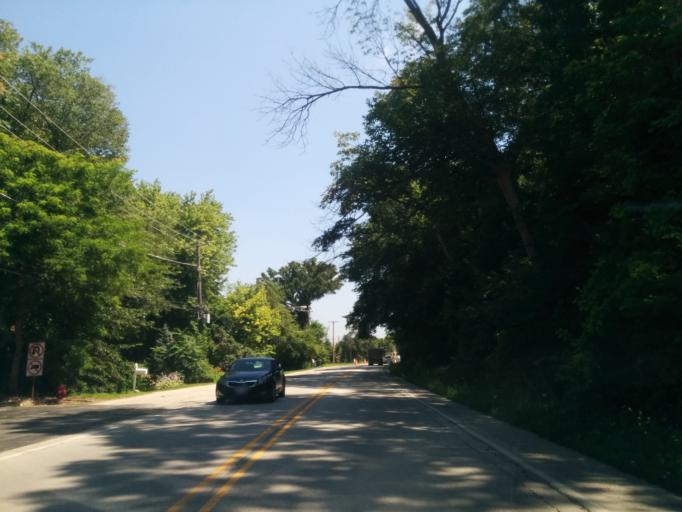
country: US
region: Illinois
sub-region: Cook County
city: Willow Springs
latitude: 41.7295
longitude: -87.8803
